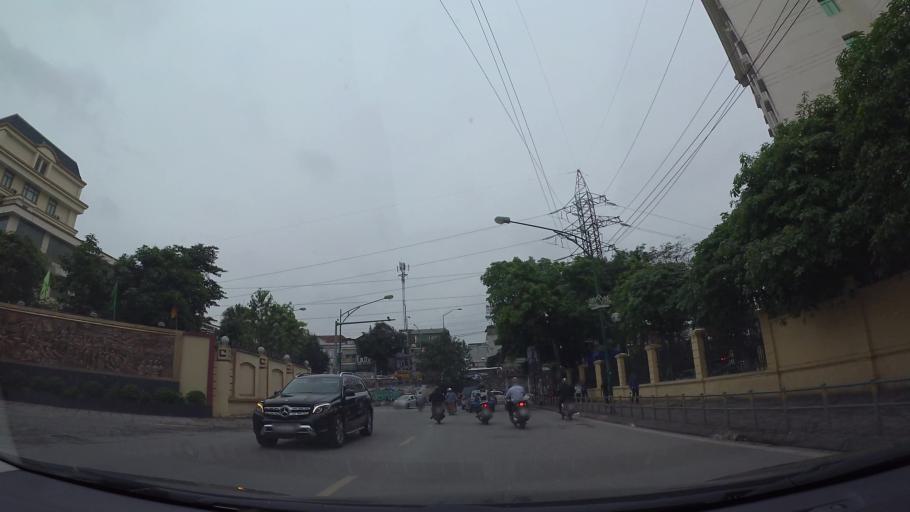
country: VN
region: Ha Noi
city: Hai BaTrung
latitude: 21.0184
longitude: 105.8613
